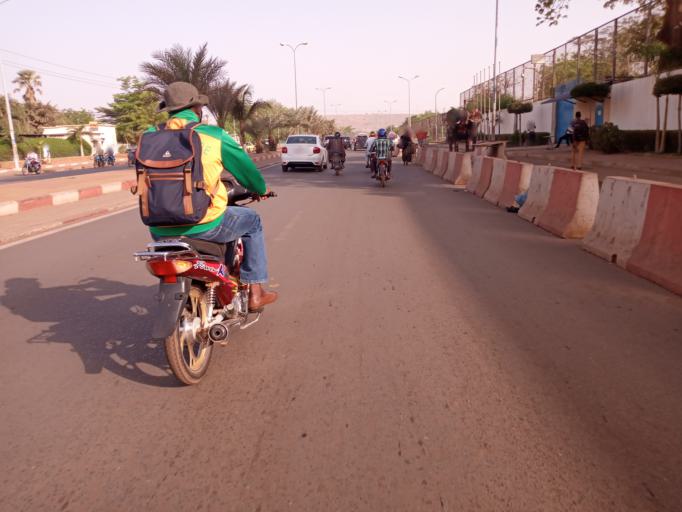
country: ML
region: Bamako
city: Bamako
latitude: 12.6378
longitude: -8.0049
